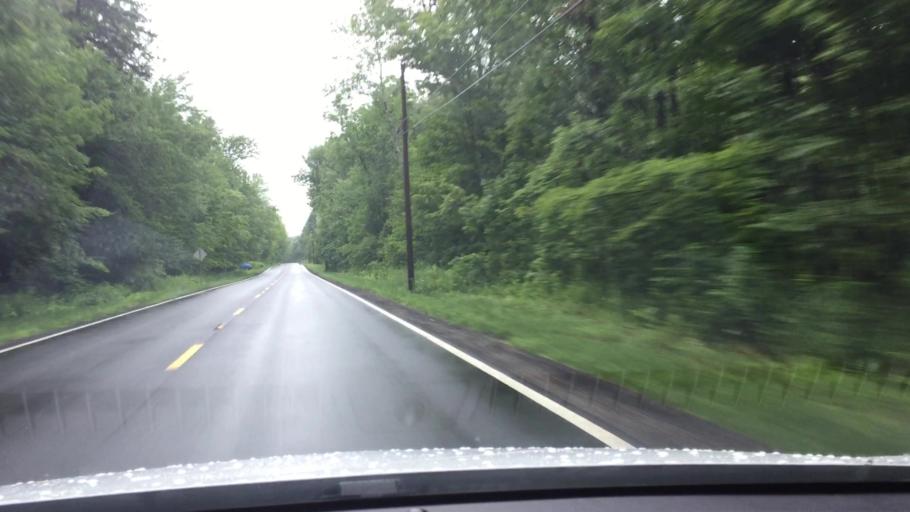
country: US
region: Massachusetts
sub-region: Berkshire County
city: Becket
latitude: 42.3525
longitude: -73.1275
